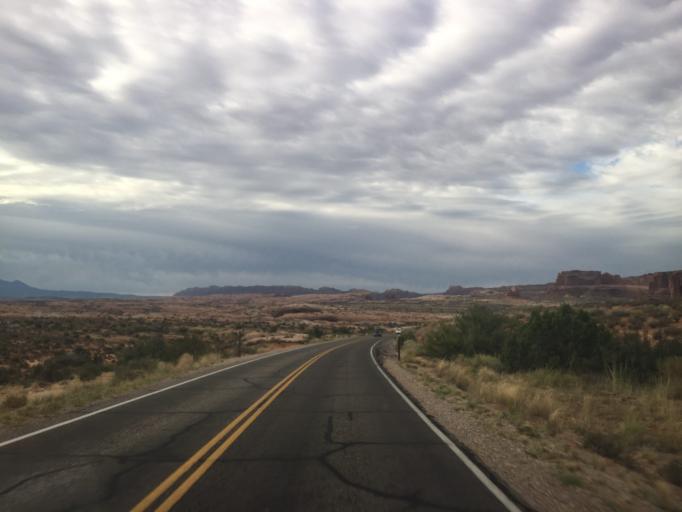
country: US
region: Utah
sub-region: Grand County
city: Moab
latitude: 38.6609
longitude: -109.5881
